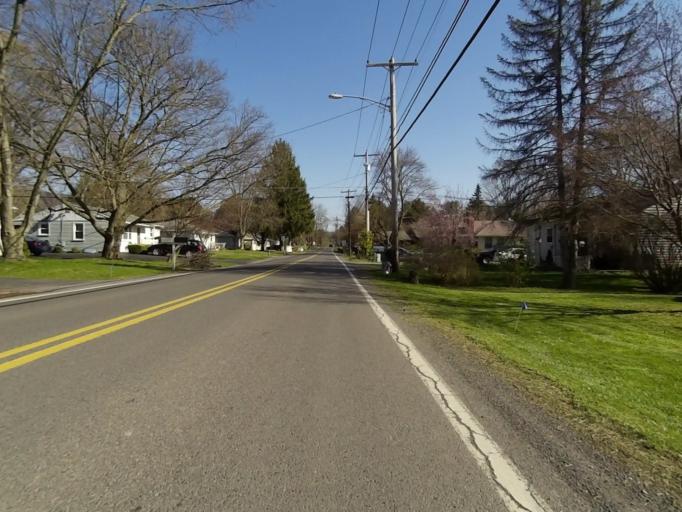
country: US
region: Pennsylvania
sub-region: Centre County
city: Houserville
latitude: 40.8250
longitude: -77.8297
